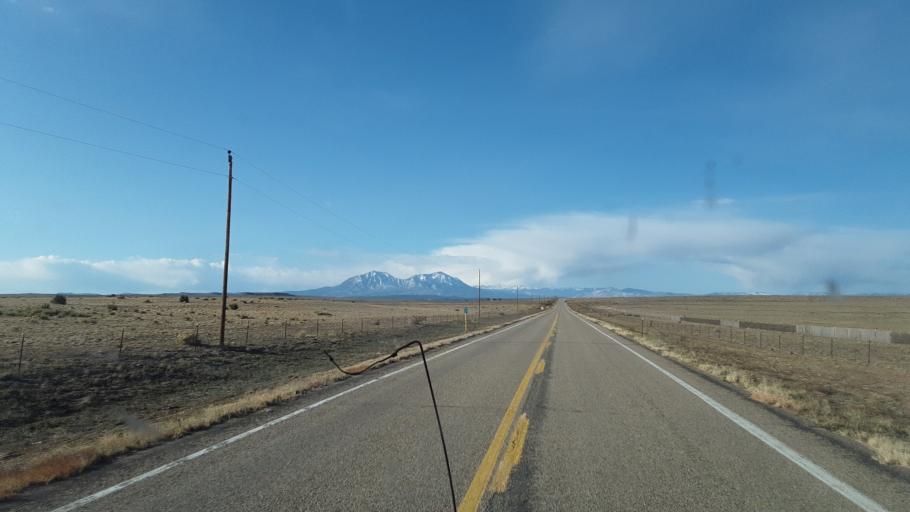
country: US
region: Colorado
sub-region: Huerfano County
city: Walsenburg
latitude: 37.6786
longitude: -104.6562
